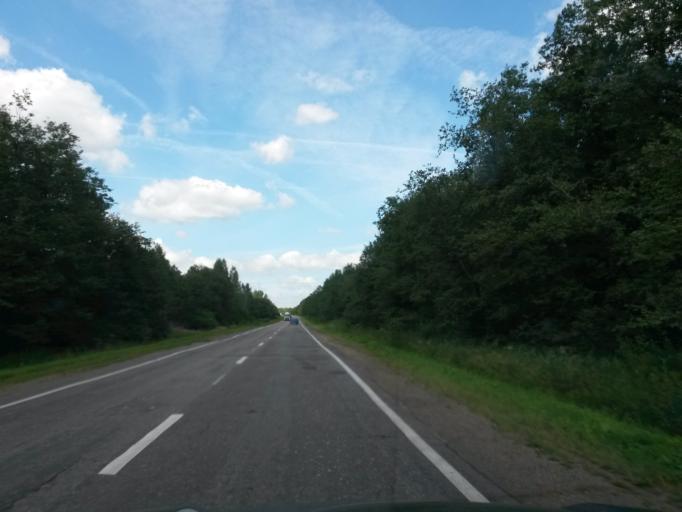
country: RU
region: Jaroslavl
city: Gavrilov-Yam
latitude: 57.4352
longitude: 39.9179
